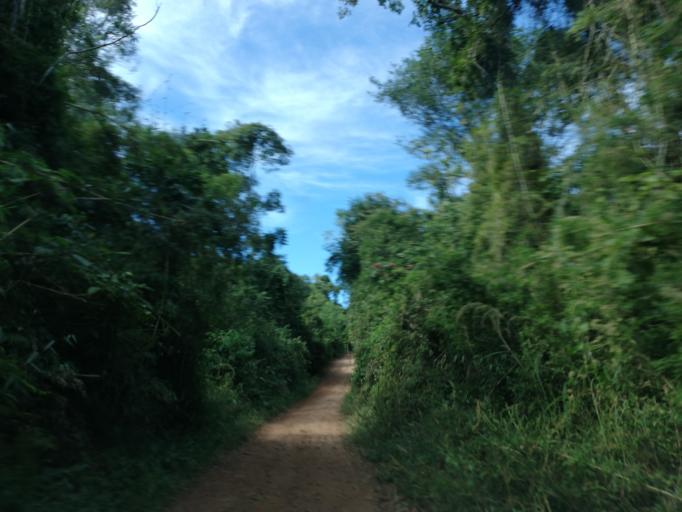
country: AR
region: Misiones
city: Dos de Mayo
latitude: -27.0141
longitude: -54.4340
